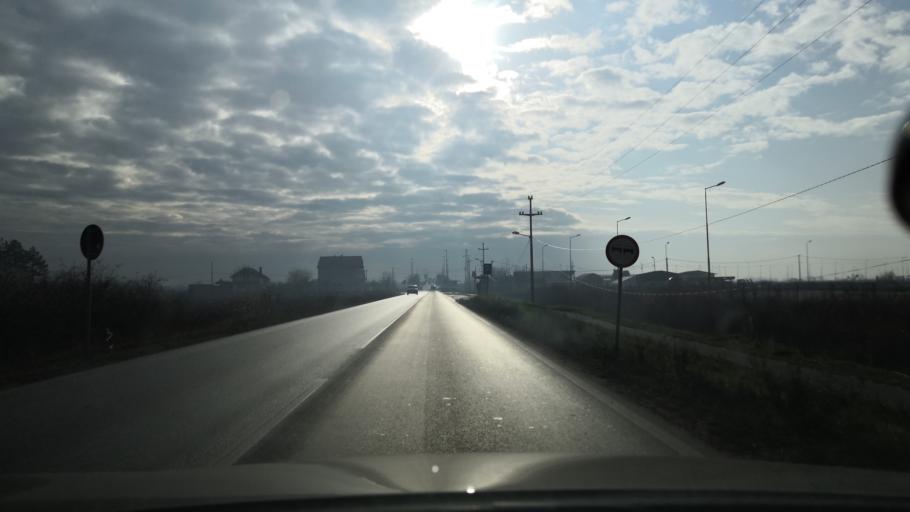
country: RS
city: Dobanovci
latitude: 44.8496
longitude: 20.2079
